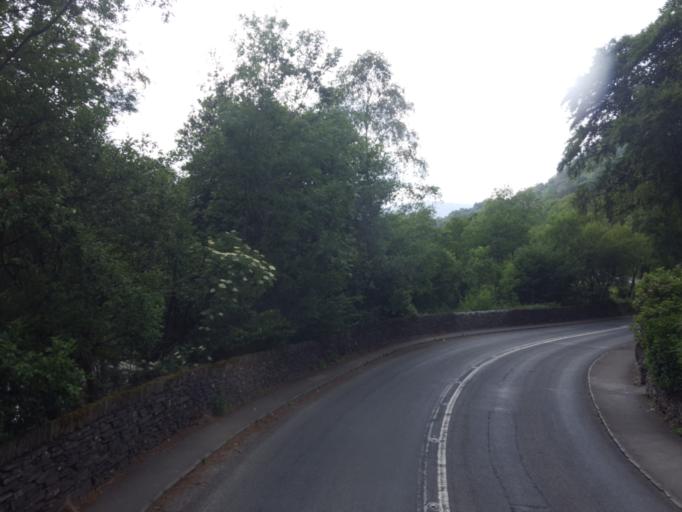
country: GB
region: England
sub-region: Cumbria
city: Ambleside
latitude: 54.4468
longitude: -2.9832
